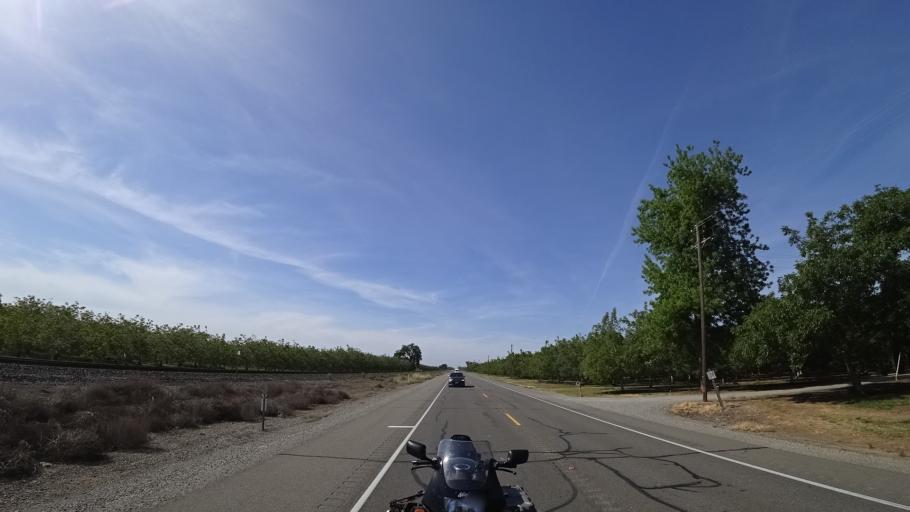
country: US
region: California
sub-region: Tehama County
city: Los Molinos
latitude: 39.9893
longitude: -122.0837
